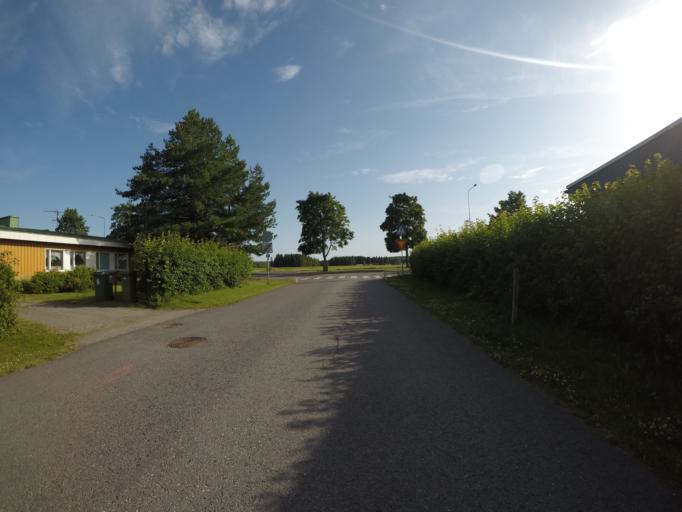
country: FI
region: Haeme
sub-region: Haemeenlinna
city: Haemeenlinna
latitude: 60.9777
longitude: 24.4195
